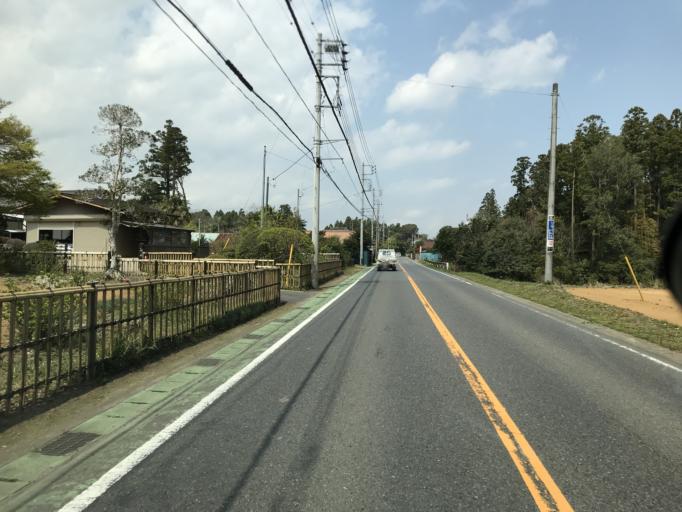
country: JP
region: Chiba
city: Sawara
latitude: 35.8689
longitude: 140.5398
